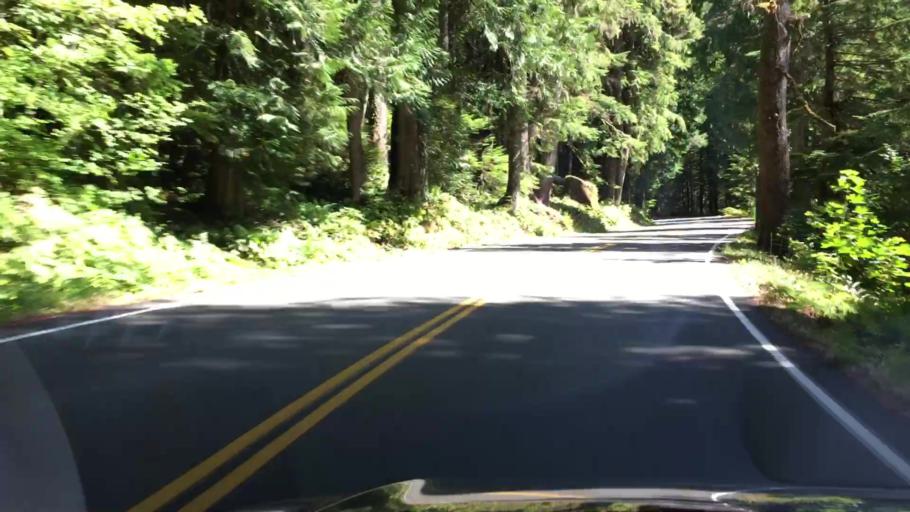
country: US
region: Washington
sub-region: Pierce County
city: Eatonville
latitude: 46.7402
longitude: -121.8819
